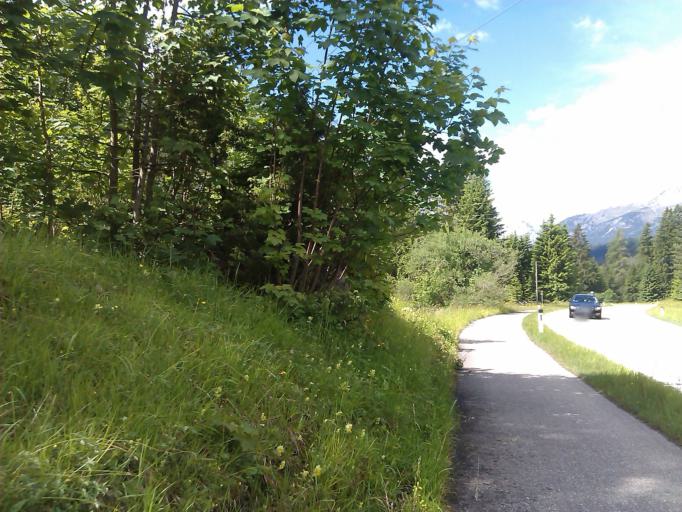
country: AT
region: Tyrol
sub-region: Politischer Bezirk Reutte
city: Biberwier
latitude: 47.3664
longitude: 10.8799
